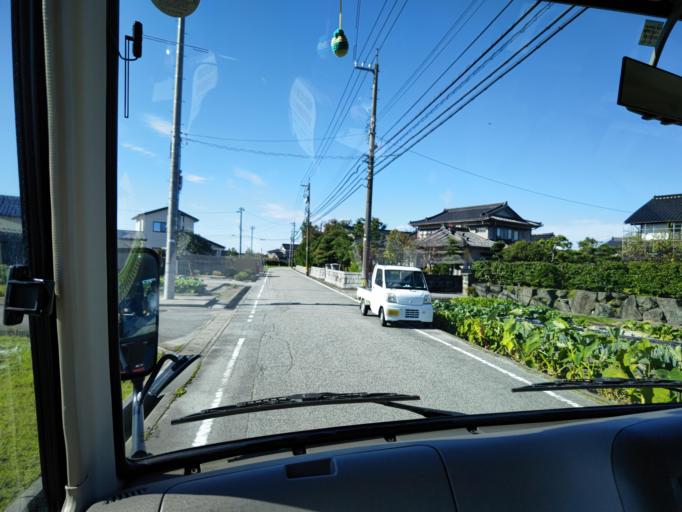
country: JP
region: Toyama
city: Nyuzen
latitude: 36.9095
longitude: 137.4309
